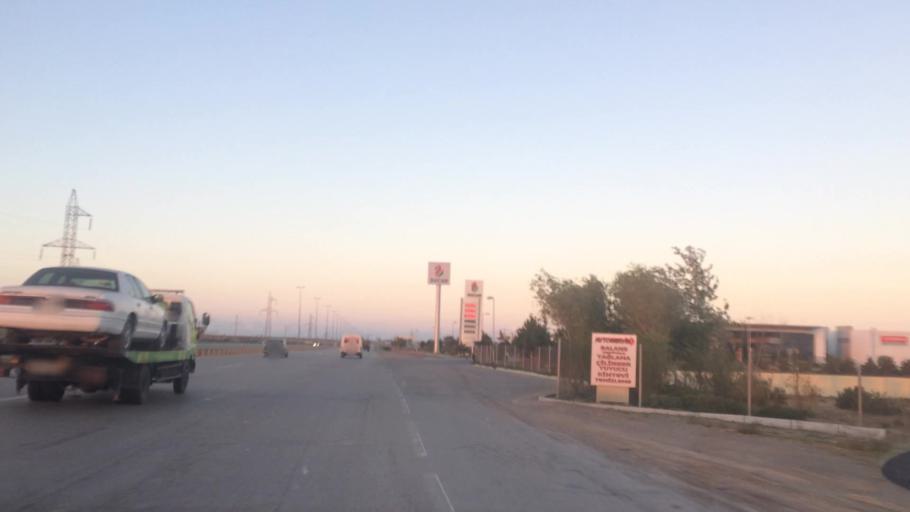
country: AZ
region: Baki
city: Qobustan
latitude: 39.9692
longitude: 49.4143
